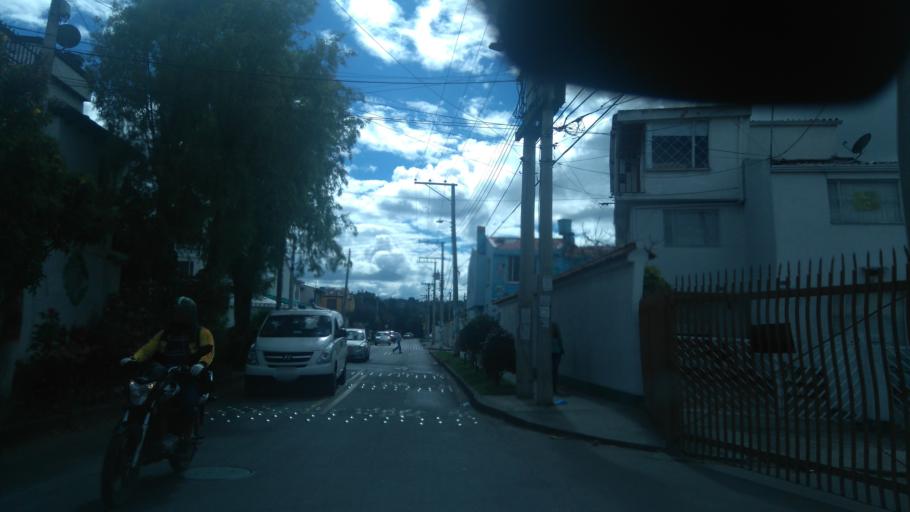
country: CO
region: Cundinamarca
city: Cota
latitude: 4.7585
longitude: -74.0545
